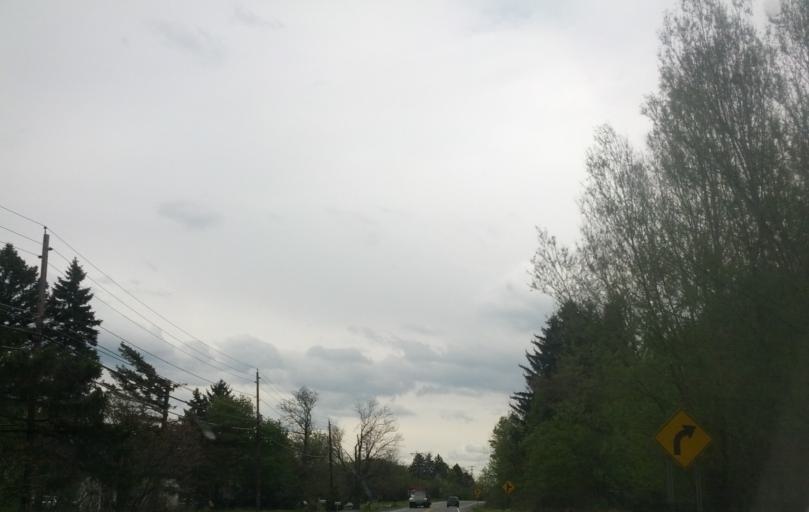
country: US
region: New York
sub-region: Onondaga County
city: Nedrow
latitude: 42.9949
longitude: -76.1010
